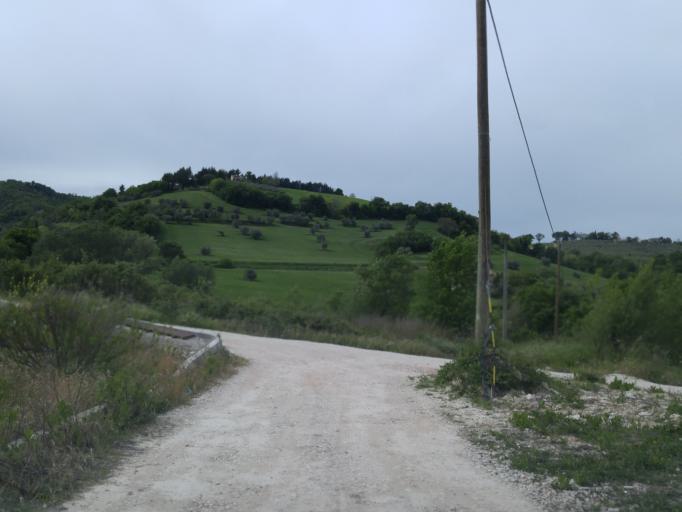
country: IT
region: The Marches
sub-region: Provincia di Pesaro e Urbino
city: Fossombrone
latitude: 43.7003
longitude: 12.8147
